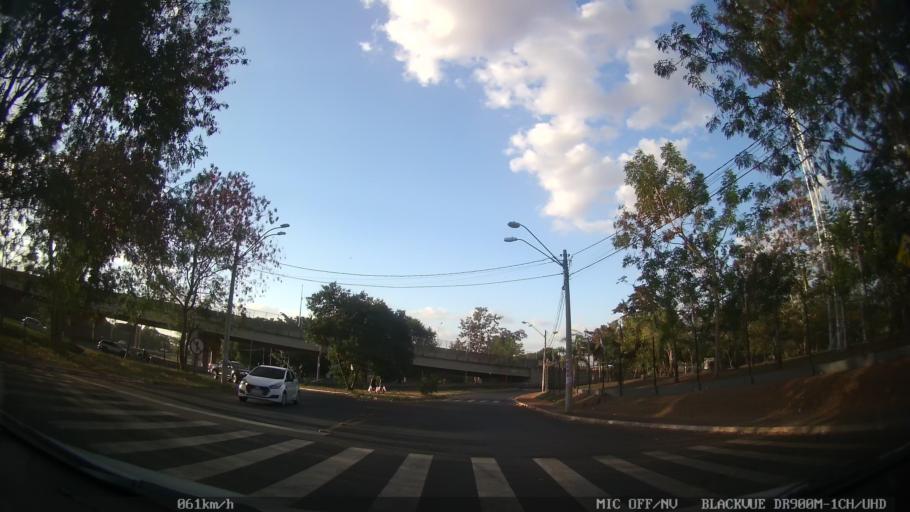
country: BR
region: Sao Paulo
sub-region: Ribeirao Preto
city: Ribeirao Preto
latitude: -21.1942
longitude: -47.7569
